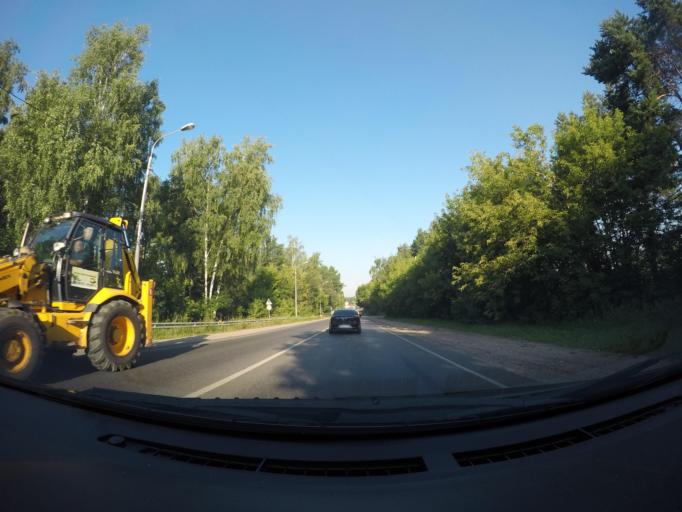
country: RU
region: Moskovskaya
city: Malakhovka
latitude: 55.6590
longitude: 38.0313
